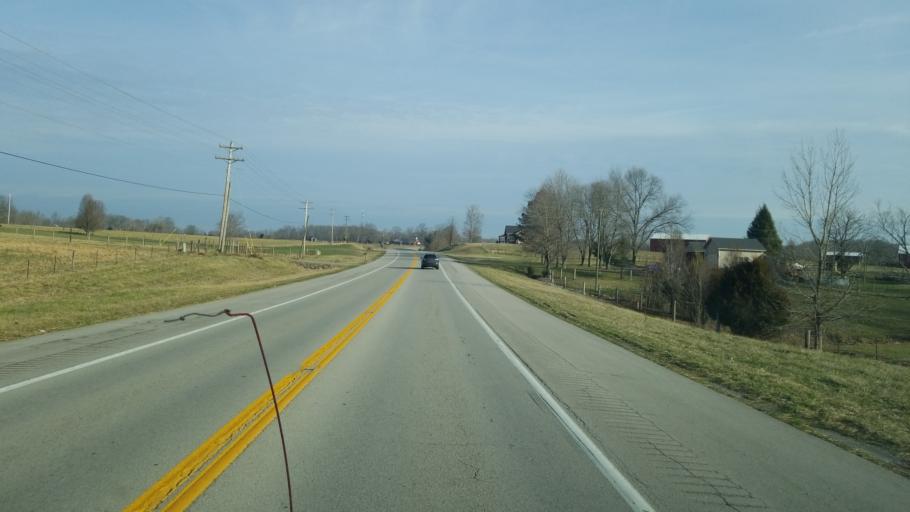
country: US
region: Kentucky
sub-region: Russell County
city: Russell Springs
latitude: 37.1152
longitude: -85.0492
